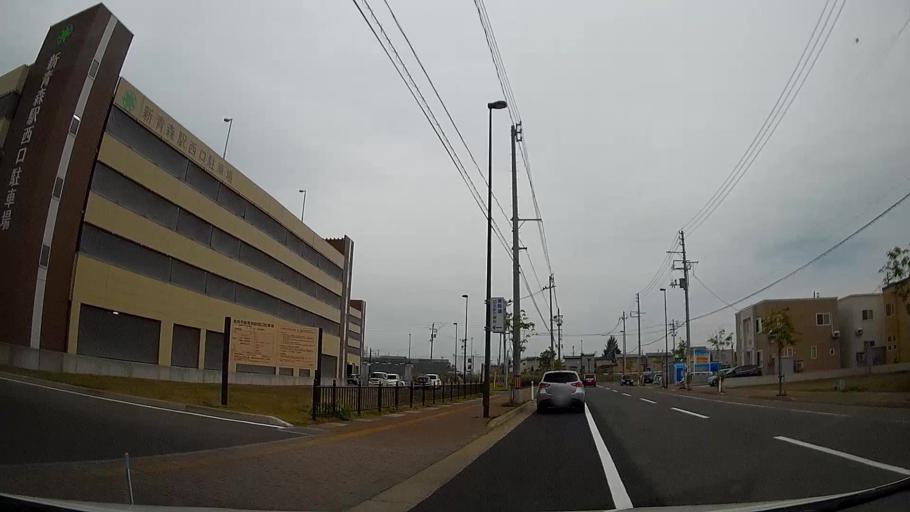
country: JP
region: Aomori
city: Aomori Shi
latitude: 40.8290
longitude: 140.6922
